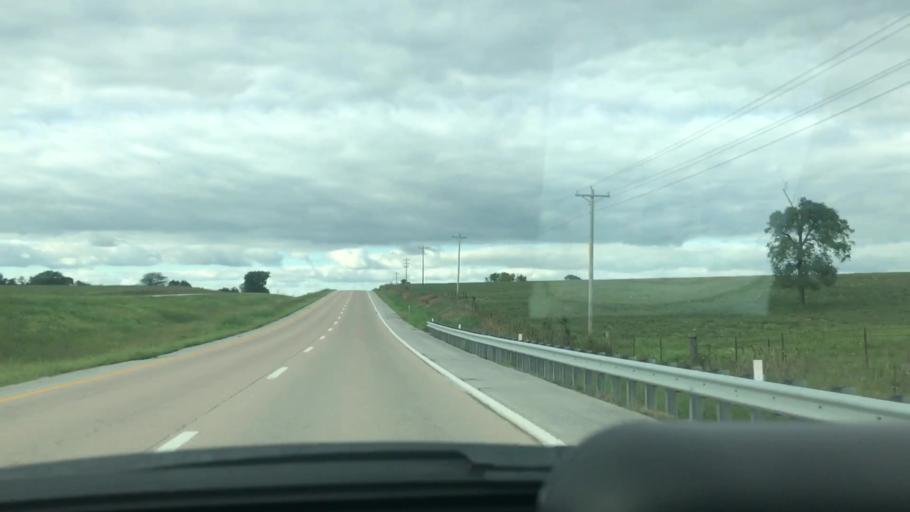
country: US
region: Missouri
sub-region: Benton County
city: Lincoln
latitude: 38.3253
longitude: -93.3418
